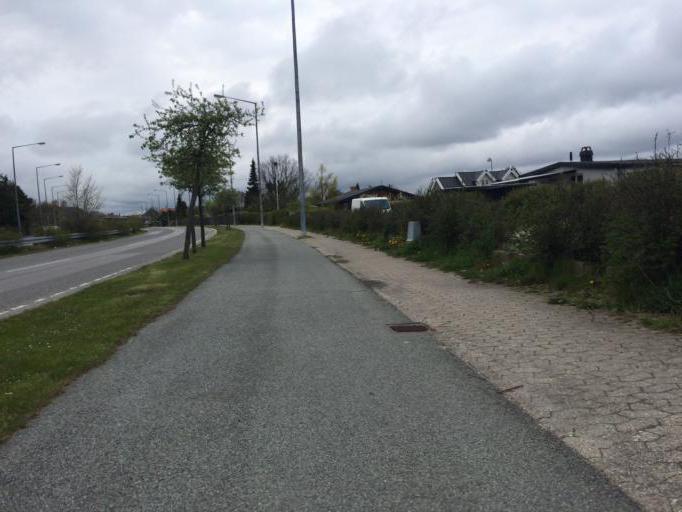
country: DK
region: Capital Region
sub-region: Vallensbaek Kommune
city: Vallensbaek
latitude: 55.6191
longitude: 12.3938
